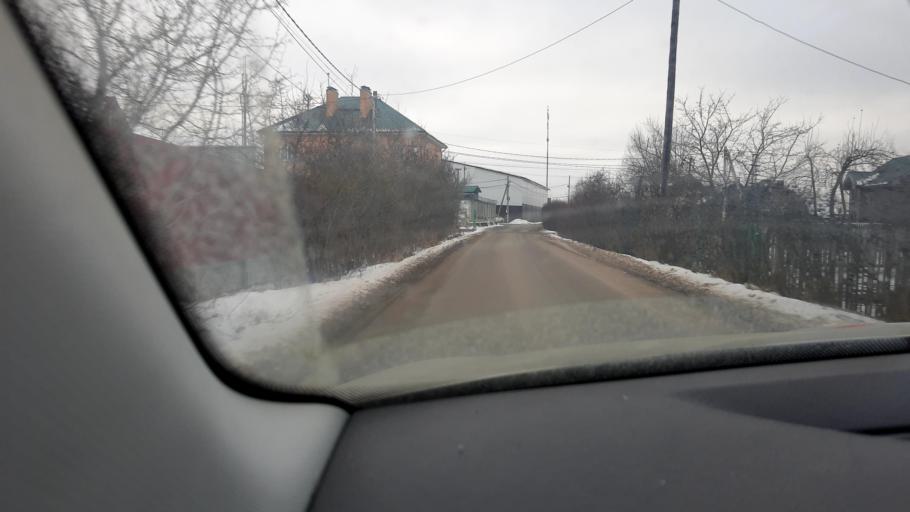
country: RU
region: Moskovskaya
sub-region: Leninskiy Rayon
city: Molokovo
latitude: 55.4907
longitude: 37.8577
